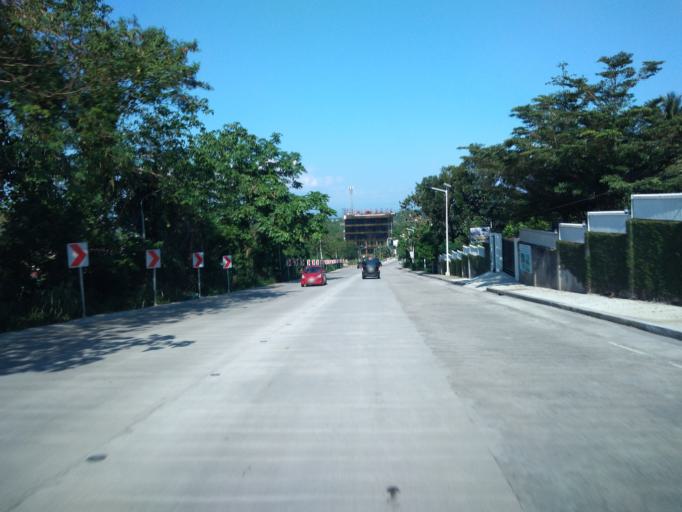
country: PH
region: Calabarzon
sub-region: Province of Laguna
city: Prinza
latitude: 14.1773
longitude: 121.1531
